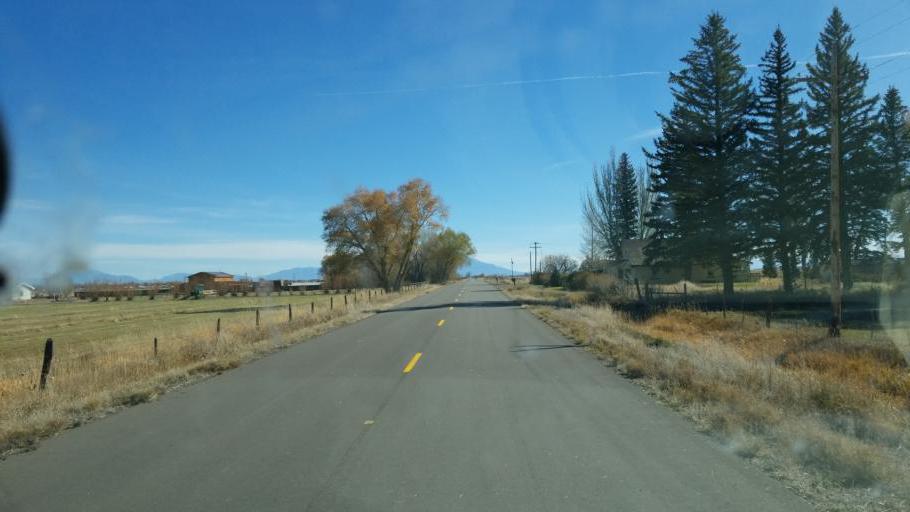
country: US
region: Colorado
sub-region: Rio Grande County
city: Monte Vista
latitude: 37.5604
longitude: -106.1785
